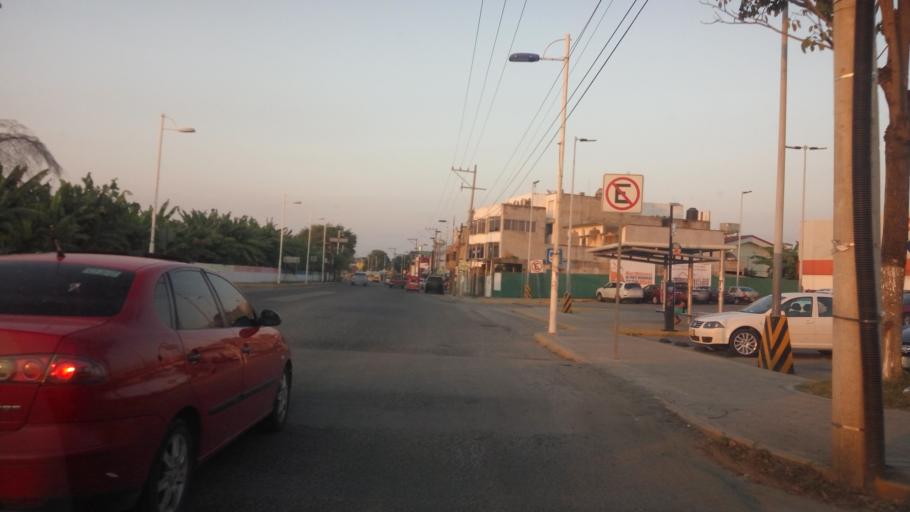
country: MX
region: Tabasco
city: Villahermosa
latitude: 17.9876
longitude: -92.9155
